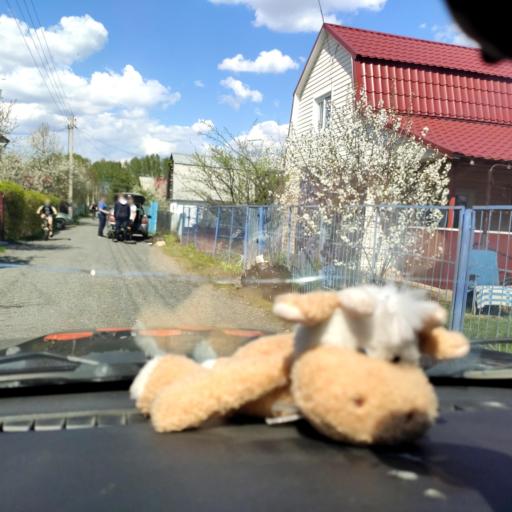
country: RU
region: Samara
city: Podstepki
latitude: 53.6053
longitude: 49.2205
